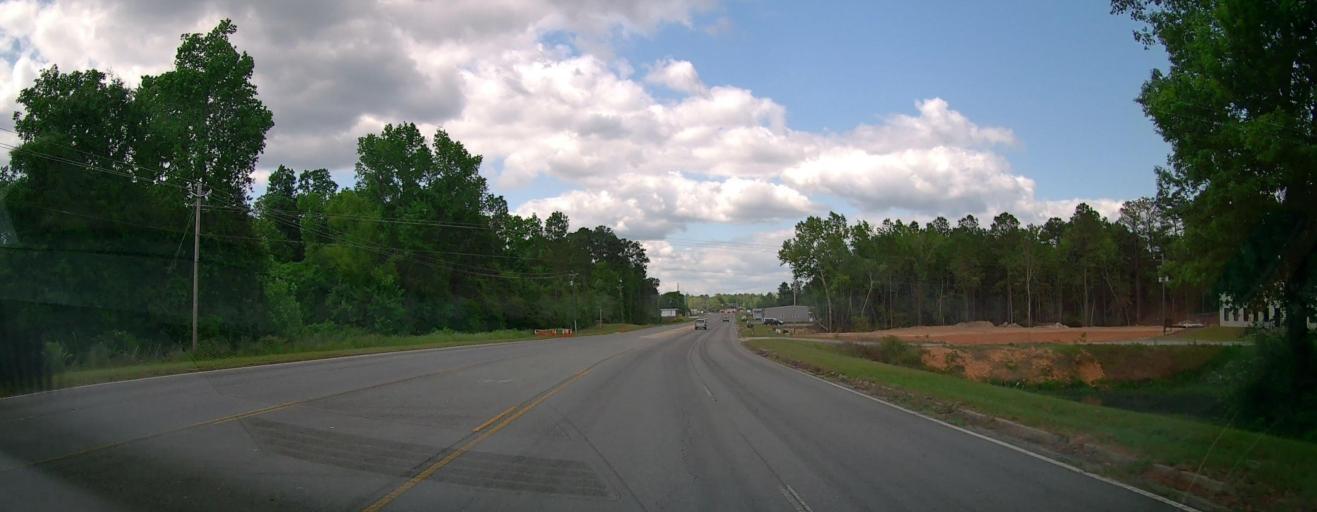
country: US
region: Georgia
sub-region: Laurens County
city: East Dublin
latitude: 32.5403
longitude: -82.8828
